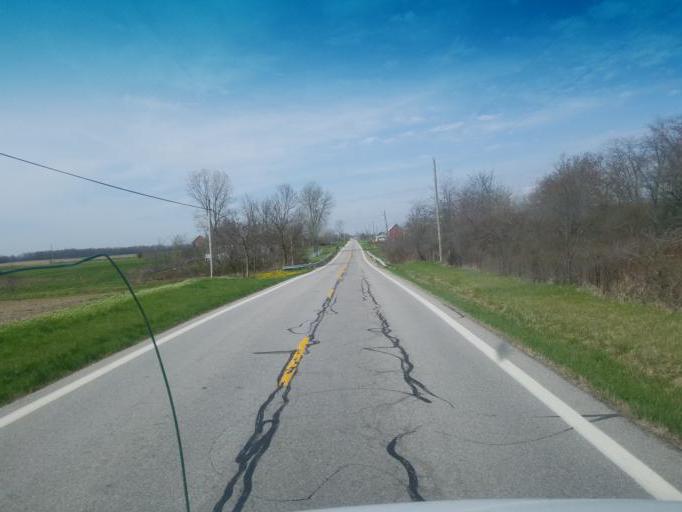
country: US
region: Ohio
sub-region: Union County
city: Richwood
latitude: 40.4732
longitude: -83.4228
